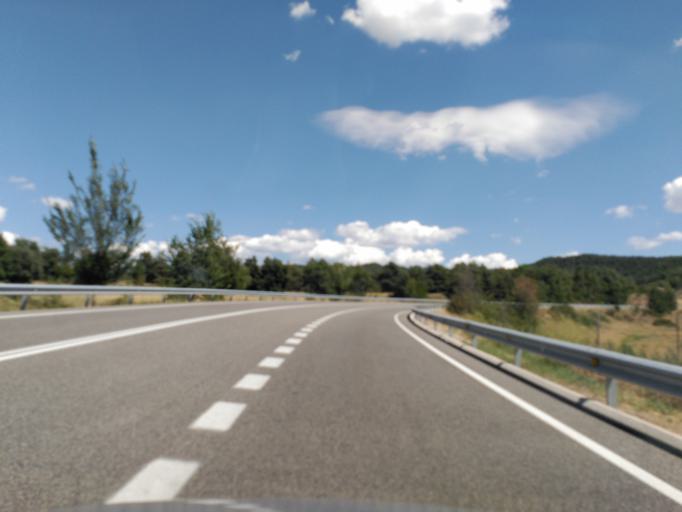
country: ES
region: Catalonia
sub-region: Provincia de Barcelona
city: Olost
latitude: 41.9722
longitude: 2.1259
